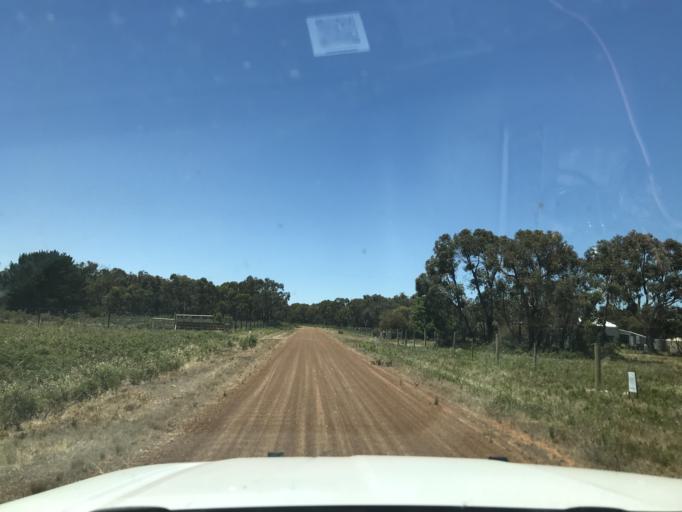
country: AU
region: South Australia
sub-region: Wattle Range
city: Penola
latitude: -37.0458
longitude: 141.3851
